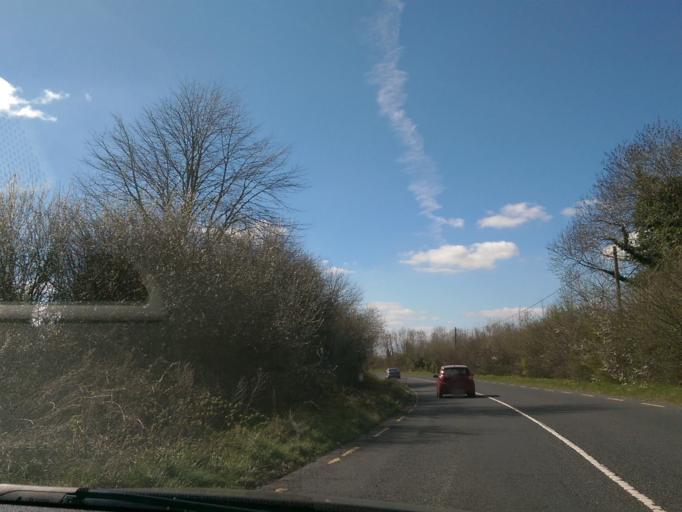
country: IE
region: Leinster
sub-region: Laois
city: Stradbally
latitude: 53.0225
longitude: -7.1002
